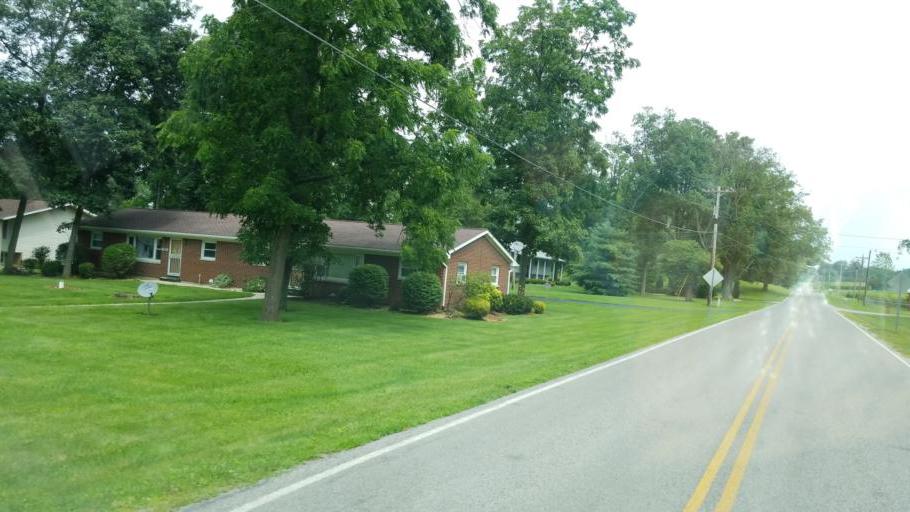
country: US
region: Ohio
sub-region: Logan County
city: Bellefontaine
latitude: 40.4118
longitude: -83.7890
